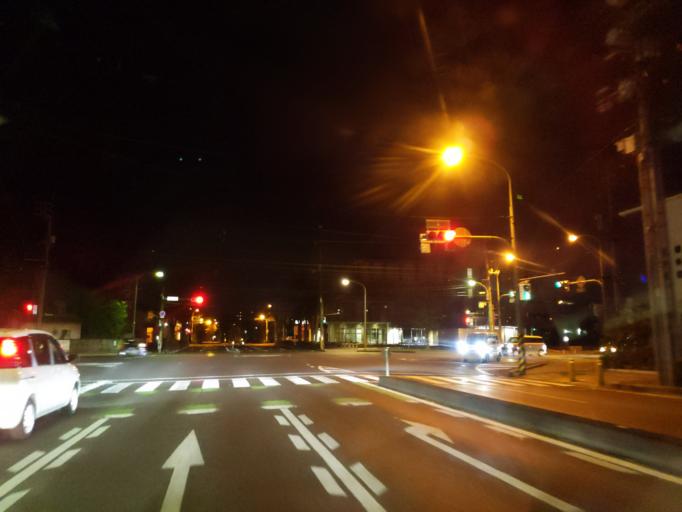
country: JP
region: Okayama
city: Okayama-shi
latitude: 34.6715
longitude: 133.9437
